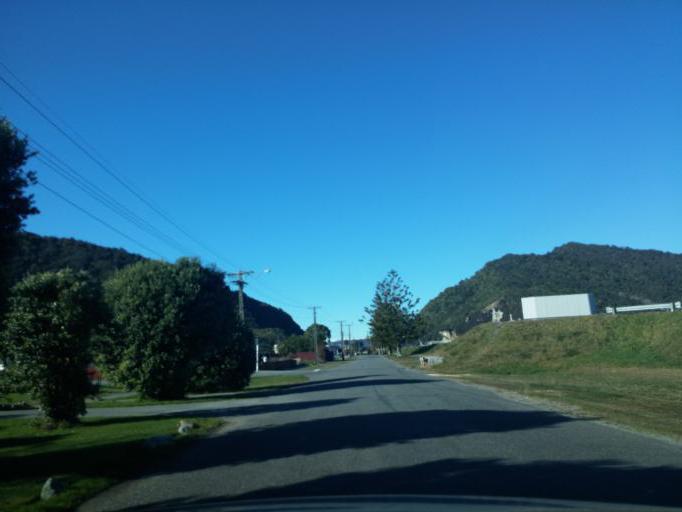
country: NZ
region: West Coast
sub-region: Grey District
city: Greymouth
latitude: -42.4420
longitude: 171.2086
